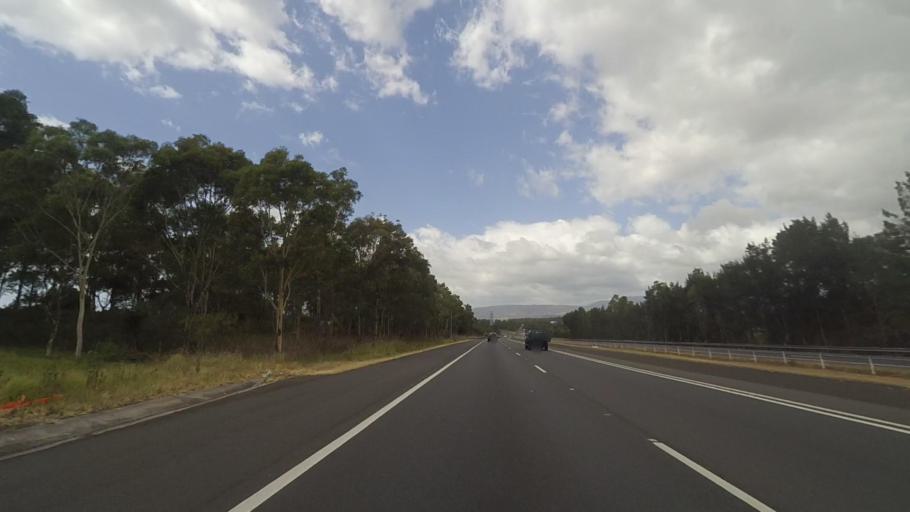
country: AU
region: New South Wales
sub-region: Wollongong
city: Dapto
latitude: -34.5214
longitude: 150.7888
